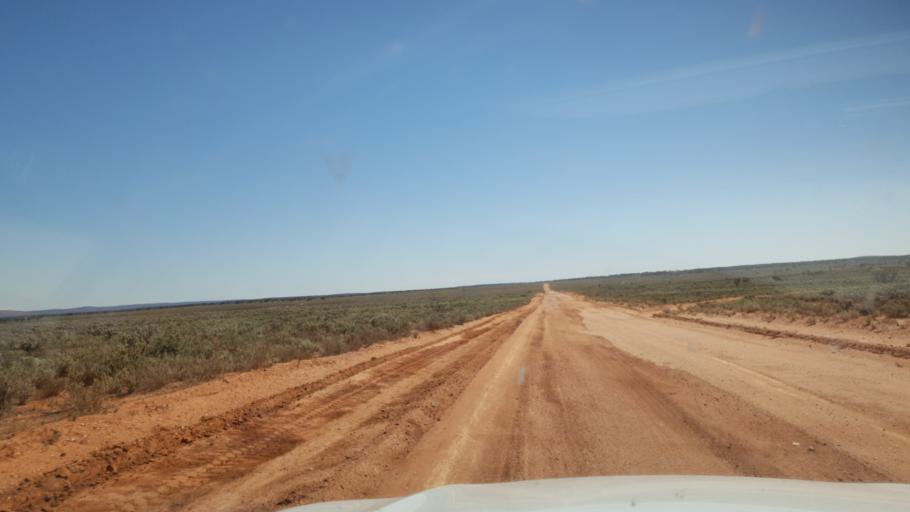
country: AU
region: South Australia
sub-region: Whyalla
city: Whyalla
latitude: -32.6376
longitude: 136.9152
